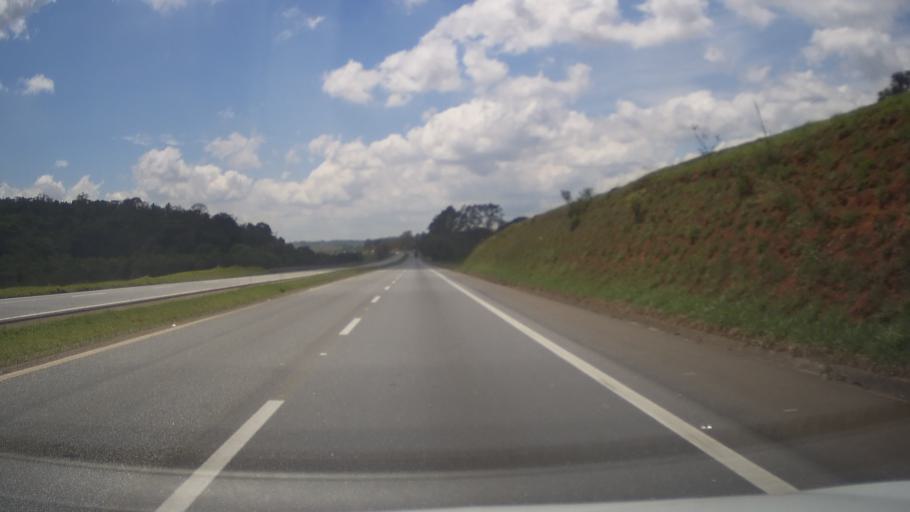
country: BR
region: Minas Gerais
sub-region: Sao Goncalo Do Sapucai
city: Sao Goncalo do Sapucai
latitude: -21.9202
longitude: -45.6073
